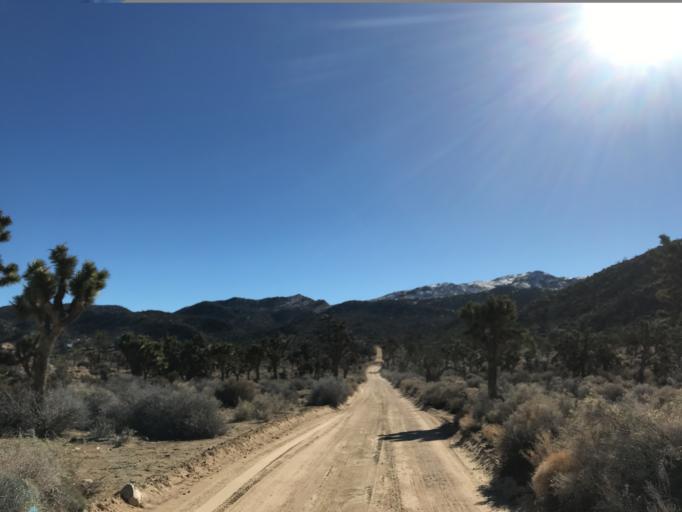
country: US
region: California
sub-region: San Bernardino County
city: Morongo Valley
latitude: 34.2294
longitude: -116.6389
